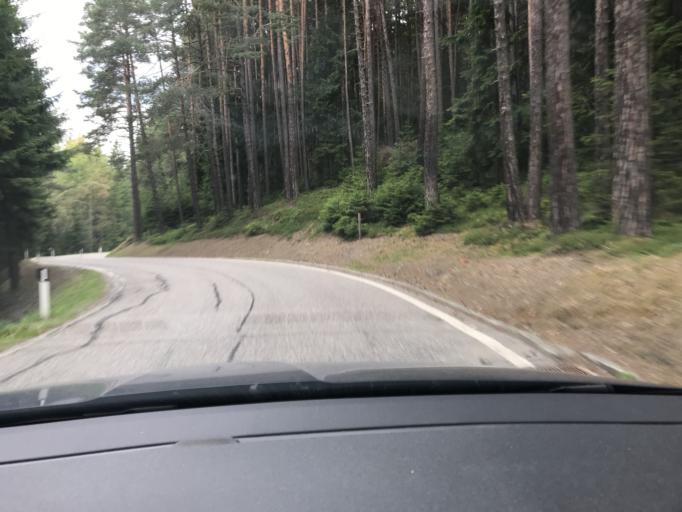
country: IT
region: Trentino-Alto Adige
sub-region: Bolzano
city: Bressanone
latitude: 46.6849
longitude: 11.6773
